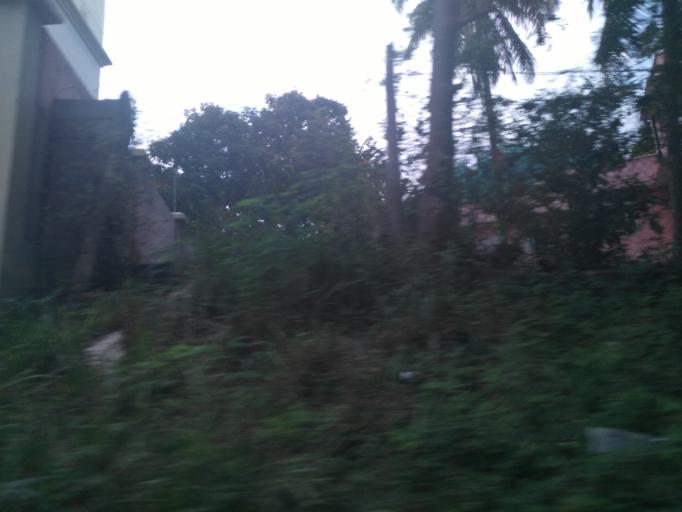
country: TZ
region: Dar es Salaam
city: Dar es Salaam
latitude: -6.7981
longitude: 39.2841
